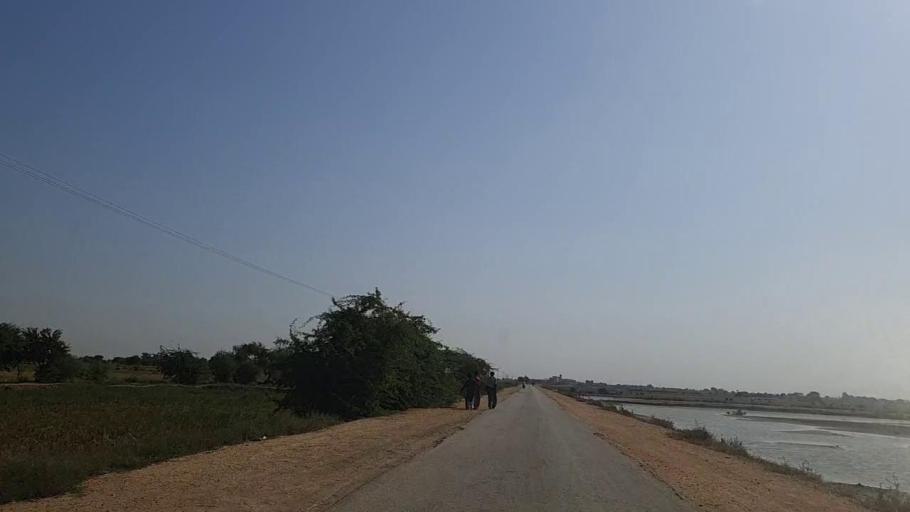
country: PK
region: Sindh
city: Mirpur Batoro
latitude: 24.6273
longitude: 68.2939
